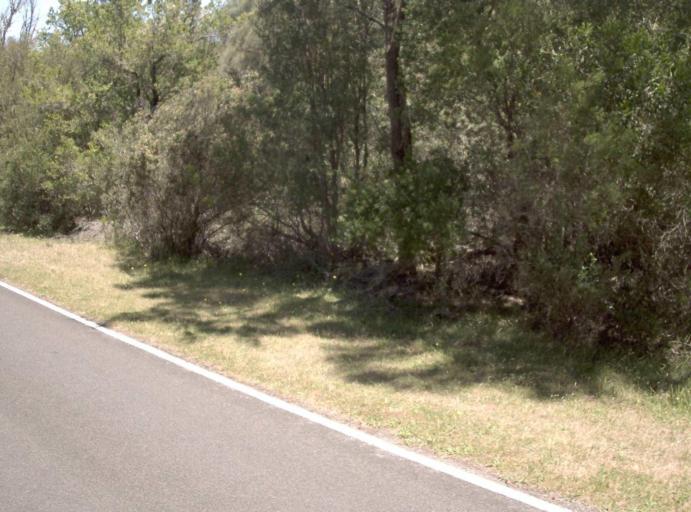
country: AU
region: Victoria
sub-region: Latrobe
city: Morwell
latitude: -38.8761
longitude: 146.2668
